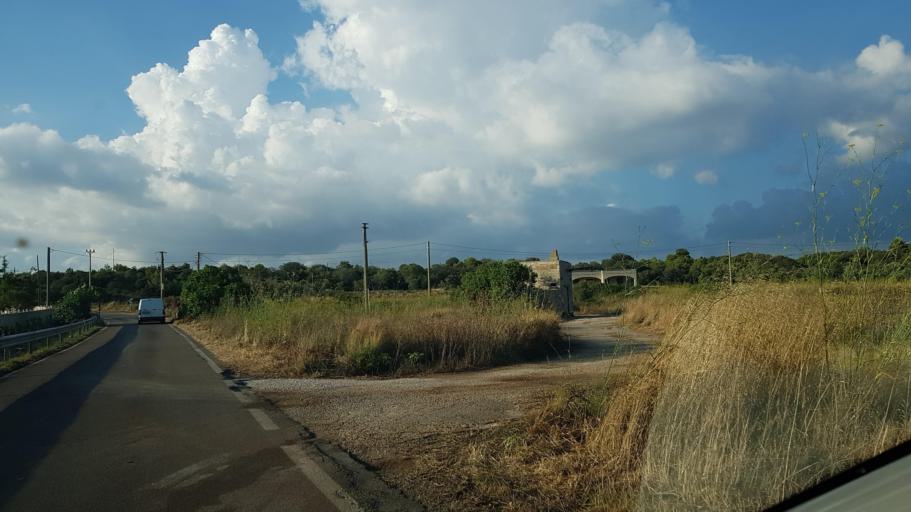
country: IT
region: Apulia
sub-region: Provincia di Lecce
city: Gemini
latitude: 39.8551
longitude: 18.2056
